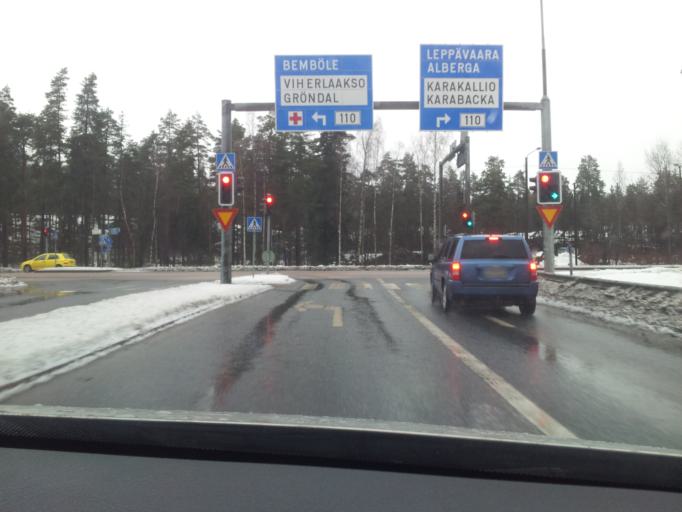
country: FI
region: Uusimaa
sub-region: Helsinki
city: Kauniainen
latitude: 60.2250
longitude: 24.7499
